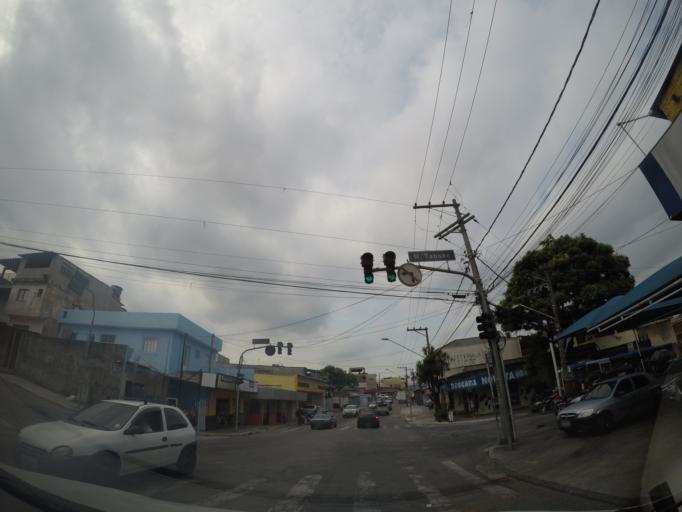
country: BR
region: Sao Paulo
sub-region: Guarulhos
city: Guarulhos
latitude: -23.4325
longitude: -46.5089
